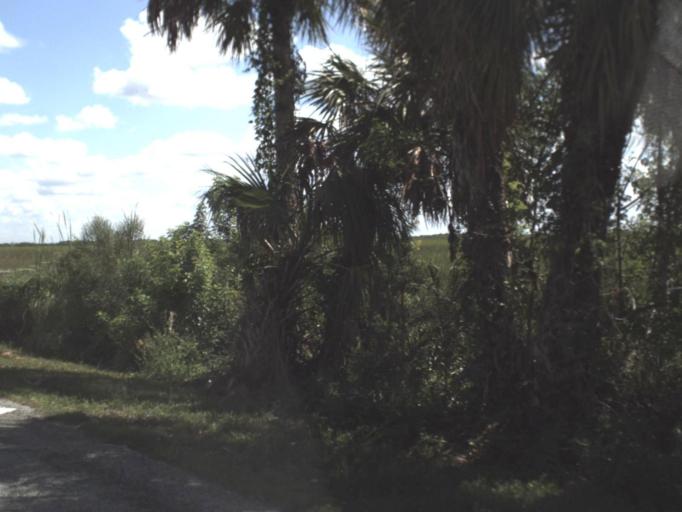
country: US
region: Florida
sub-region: Collier County
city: Marco
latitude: 25.9217
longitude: -81.4097
